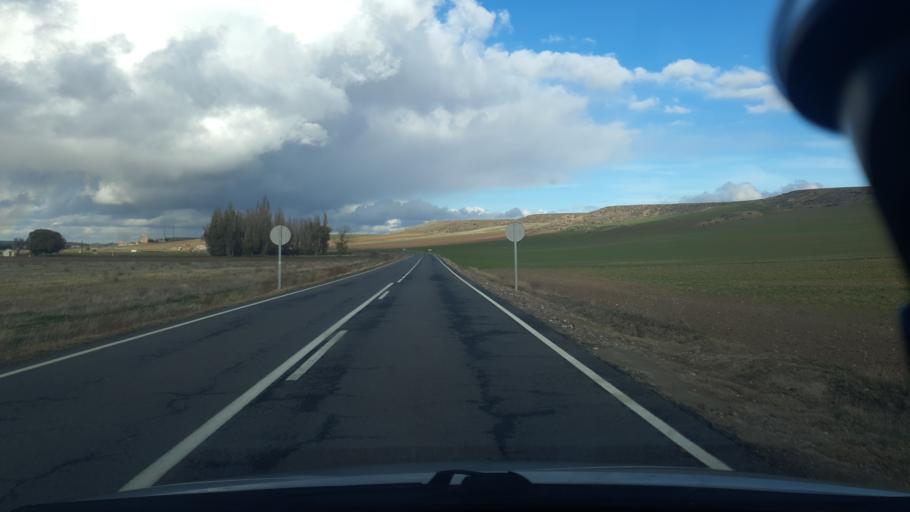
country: ES
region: Castille and Leon
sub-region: Provincia de Avila
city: Gotarrendura
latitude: 40.8394
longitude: -4.7310
